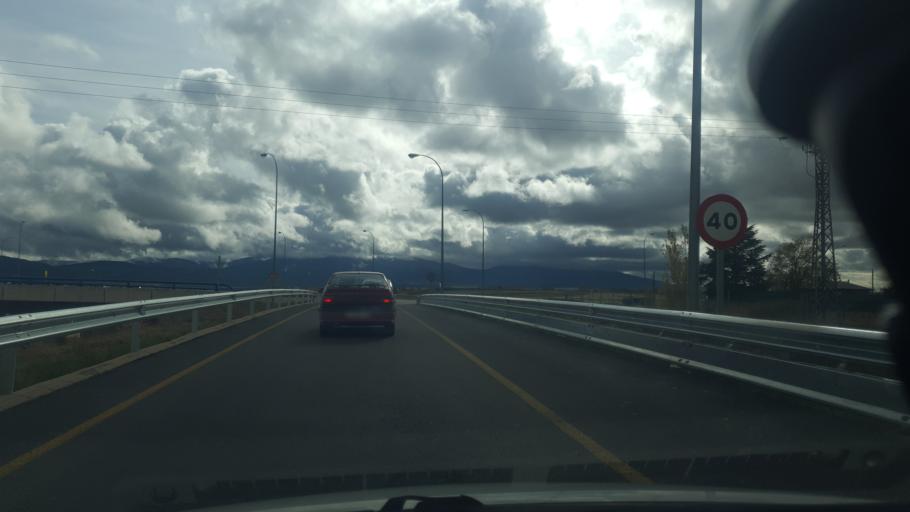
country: ES
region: Castille and Leon
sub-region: Provincia de Segovia
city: San Cristobal de Segovia
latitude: 40.9534
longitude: -4.0911
